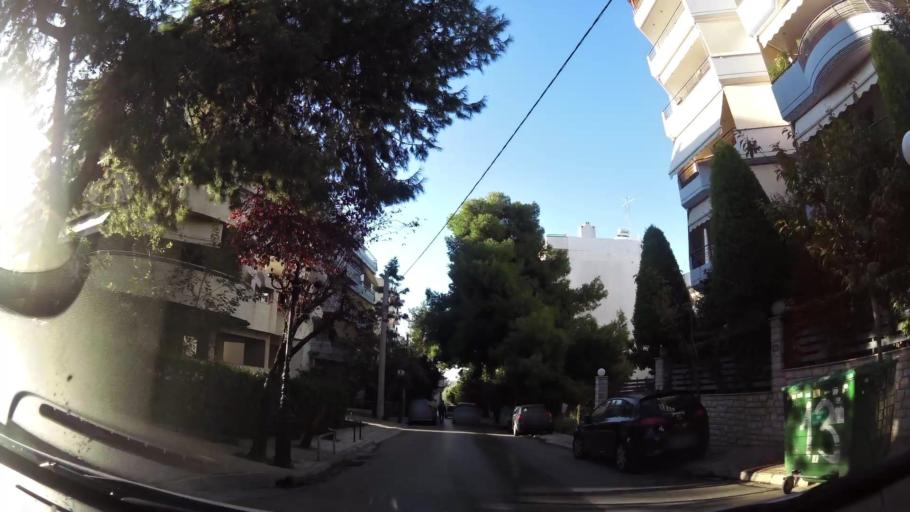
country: GR
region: Attica
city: Pefki
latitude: 38.0533
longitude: 23.7852
